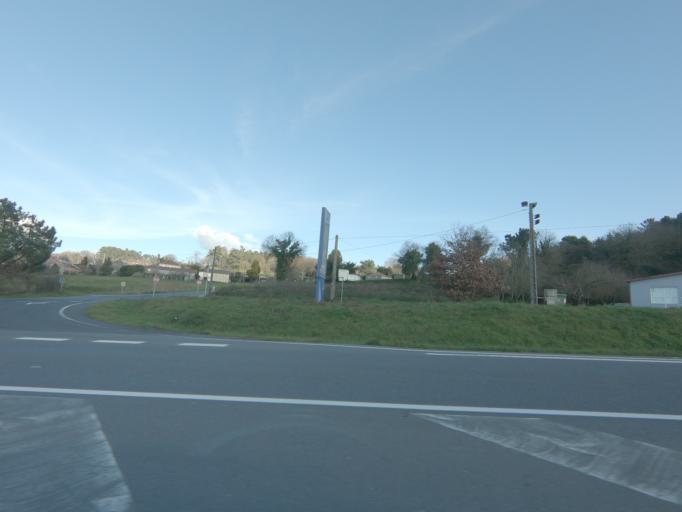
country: ES
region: Galicia
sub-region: Provincia de Pontevedra
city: Silleda
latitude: 42.7049
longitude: -8.2588
